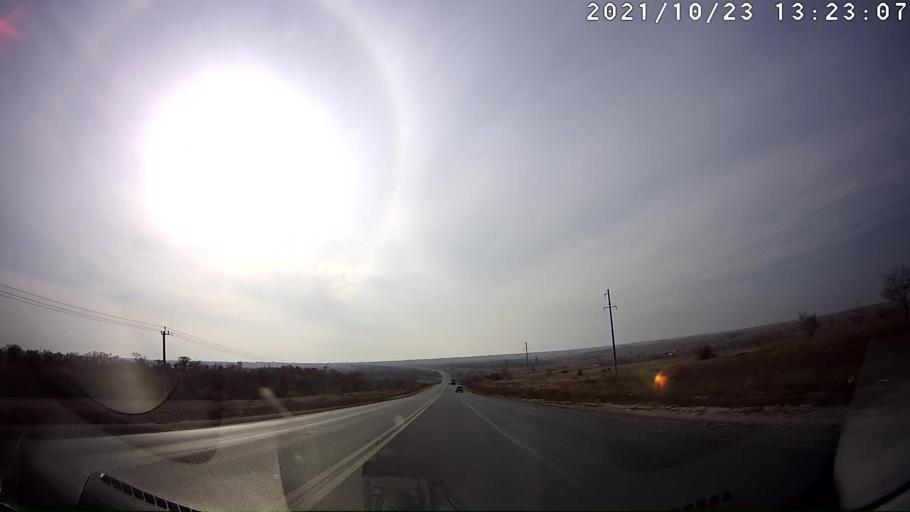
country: RU
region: Volgograd
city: Vodstroy
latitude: 48.8820
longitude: 44.5950
